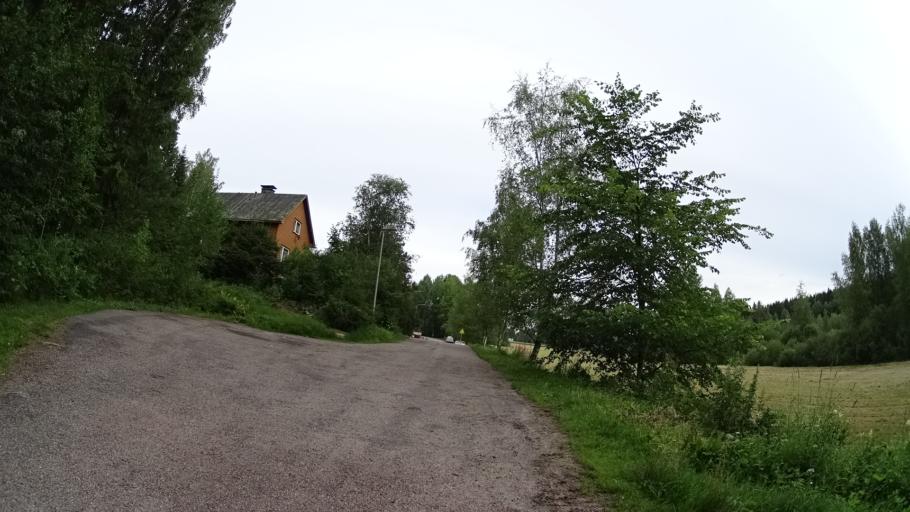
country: FI
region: Uusimaa
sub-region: Helsinki
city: Kilo
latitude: 60.2827
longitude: 24.7873
